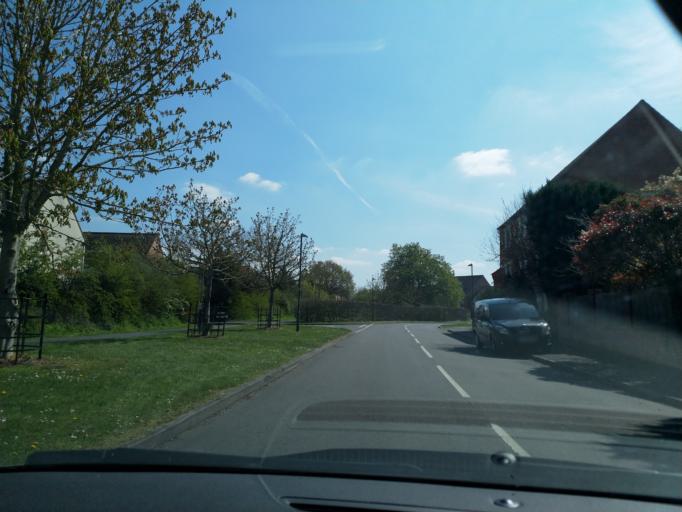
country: GB
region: England
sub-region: Warwickshire
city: Stratford-upon-Avon
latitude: 52.1843
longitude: -1.6928
